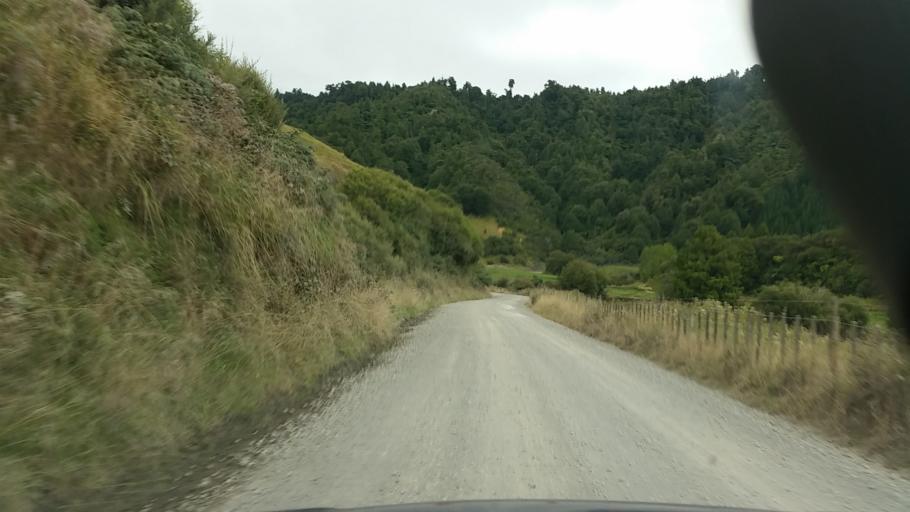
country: NZ
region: Taranaki
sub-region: South Taranaki District
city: Eltham
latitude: -39.3458
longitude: 174.5676
